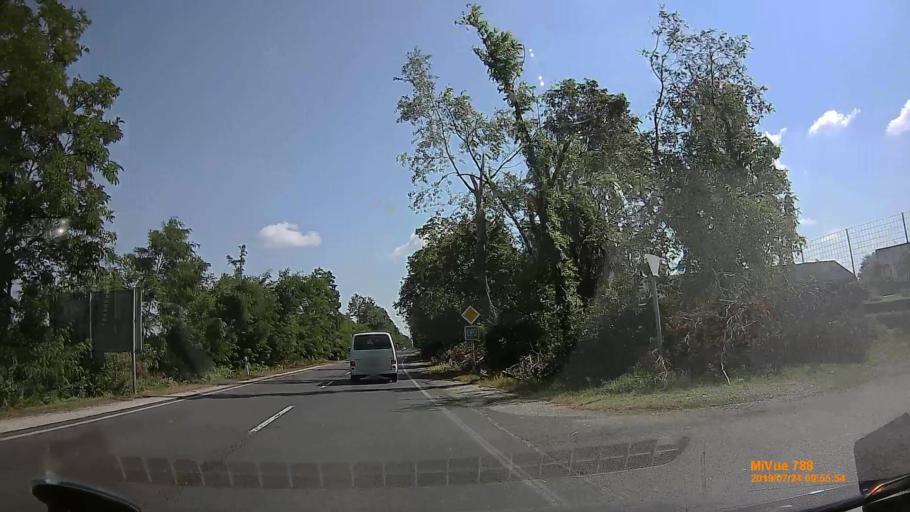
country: HU
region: Szabolcs-Szatmar-Bereg
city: Nyirmada
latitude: 48.0609
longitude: 22.2157
